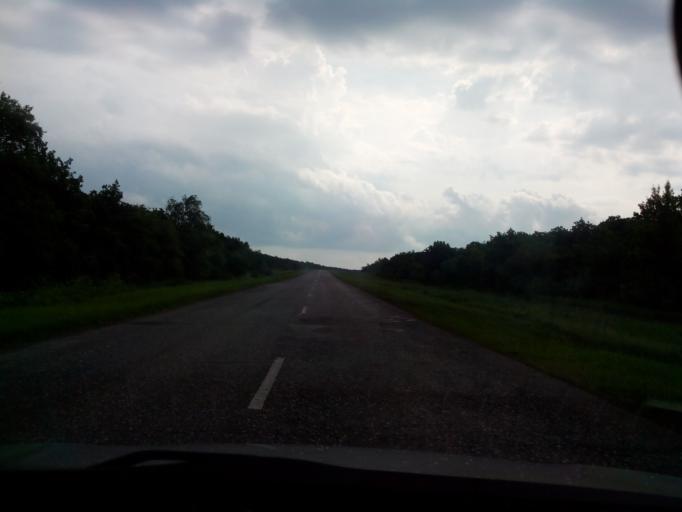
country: RU
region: Volgograd
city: Kumylzhenskaya
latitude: 49.9071
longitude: 42.8619
